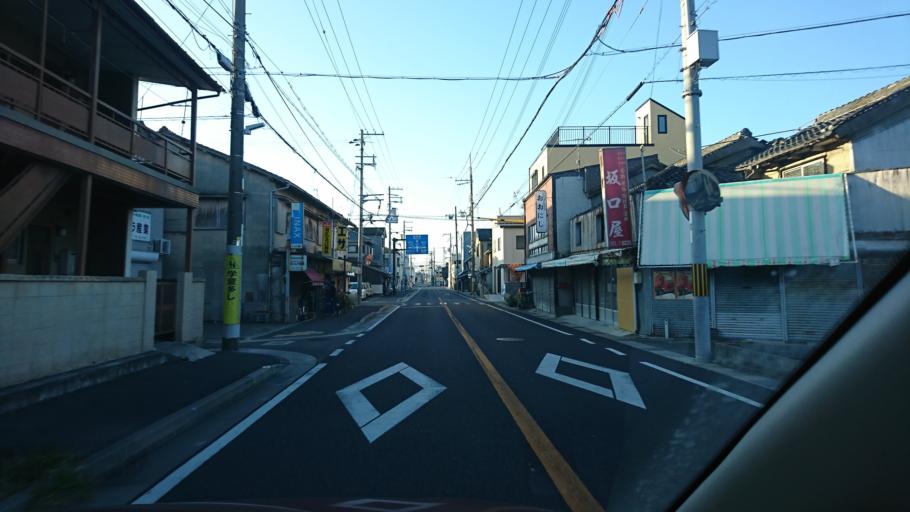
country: JP
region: Hyogo
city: Shirahamacho-usazakiminami
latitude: 34.7805
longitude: 134.7716
